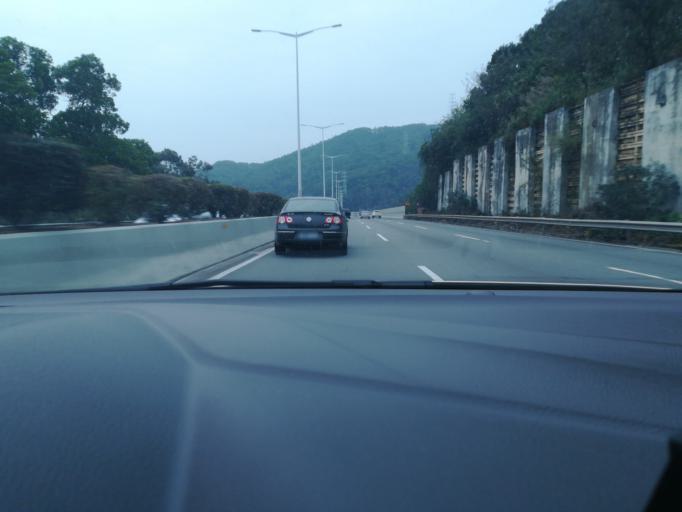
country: CN
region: Guangdong
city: Longdong
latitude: 23.2434
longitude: 113.3529
